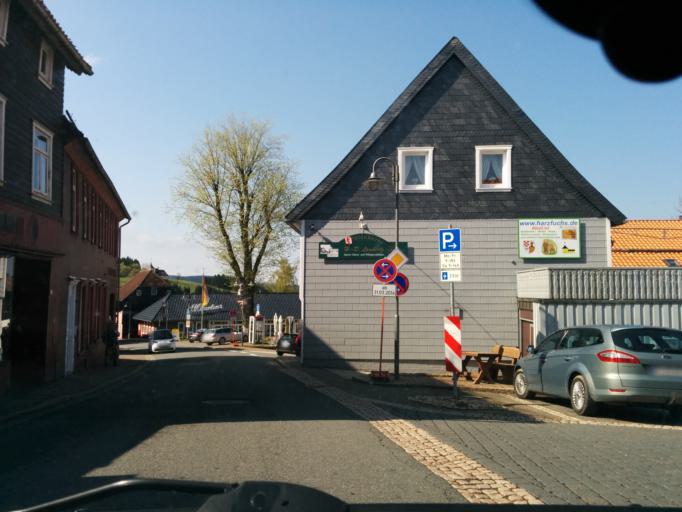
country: DE
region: Lower Saxony
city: Sankt Andreasberg
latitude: 51.7108
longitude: 10.5193
